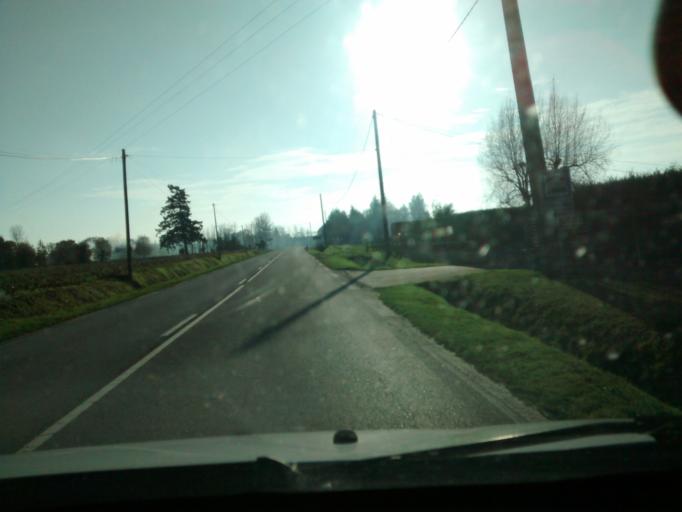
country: FR
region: Brittany
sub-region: Departement d'Ille-et-Vilaine
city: Tremblay
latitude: 48.3796
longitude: -1.4936
